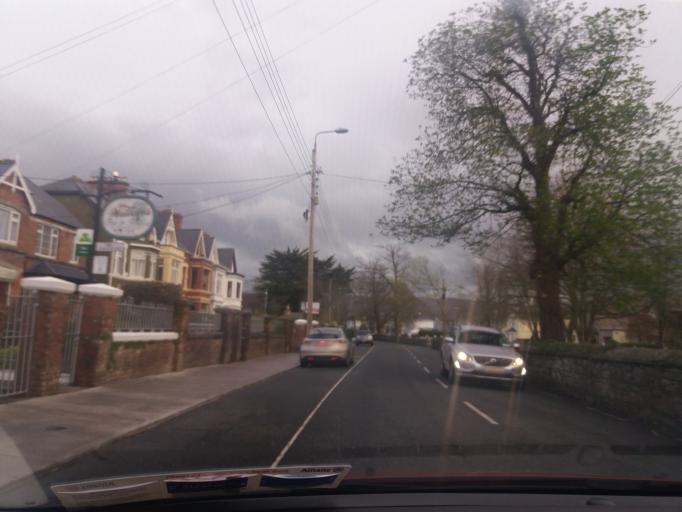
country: IE
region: Munster
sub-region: Ciarrai
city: Tralee
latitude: 52.2661
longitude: -9.6982
